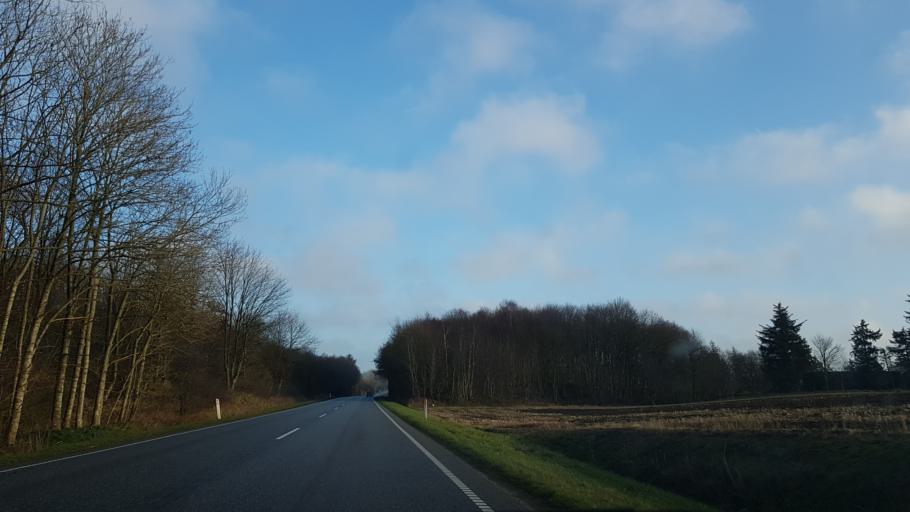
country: DK
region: South Denmark
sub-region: Haderslev Kommune
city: Vojens
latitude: 55.1727
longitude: 9.3400
